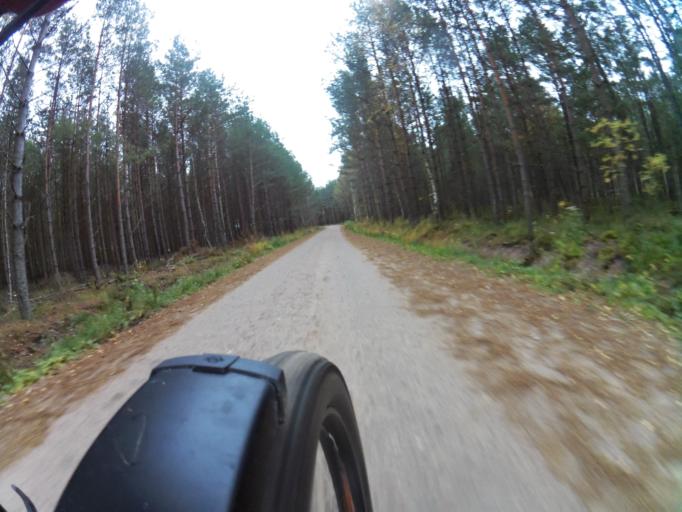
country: PL
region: Pomeranian Voivodeship
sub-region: Powiat wejherowski
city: Choczewo
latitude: 54.7822
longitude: 17.7338
